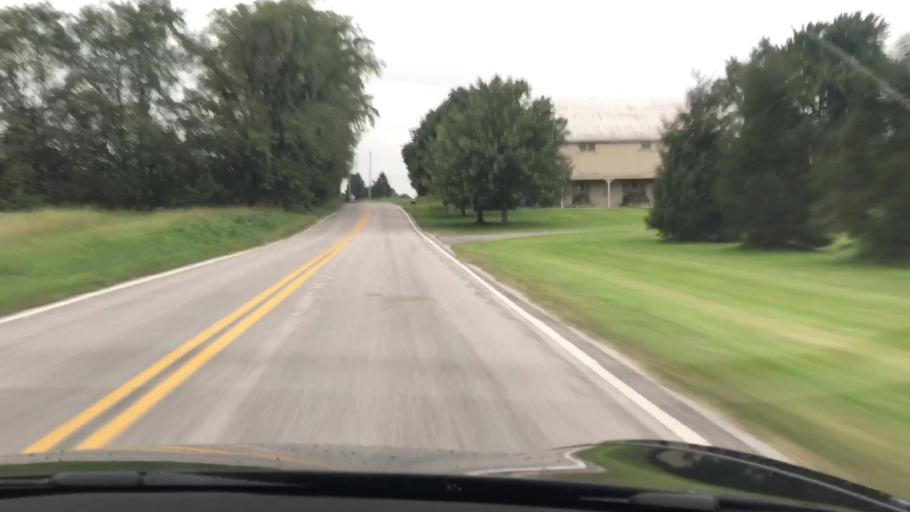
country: US
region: Pennsylvania
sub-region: York County
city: Dover
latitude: 39.9580
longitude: -76.8678
